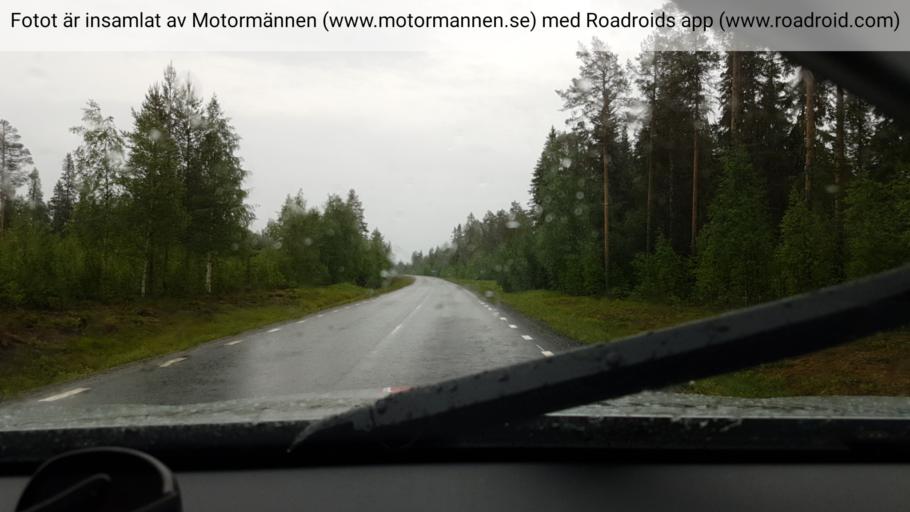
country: SE
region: Vaesterbotten
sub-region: Lycksele Kommun
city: Soderfors
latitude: 65.2554
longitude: 18.0739
